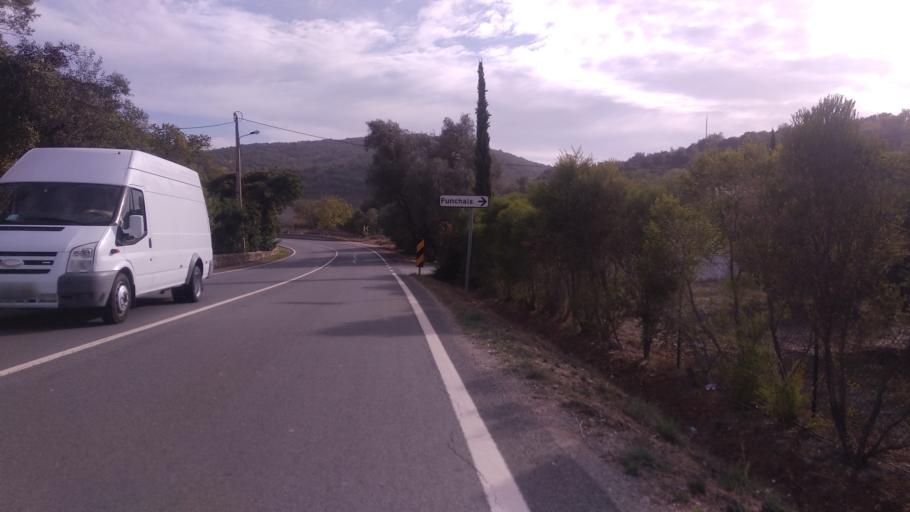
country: PT
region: Faro
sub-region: Sao Bras de Alportel
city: Sao Bras de Alportel
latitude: 37.1304
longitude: -7.8938
